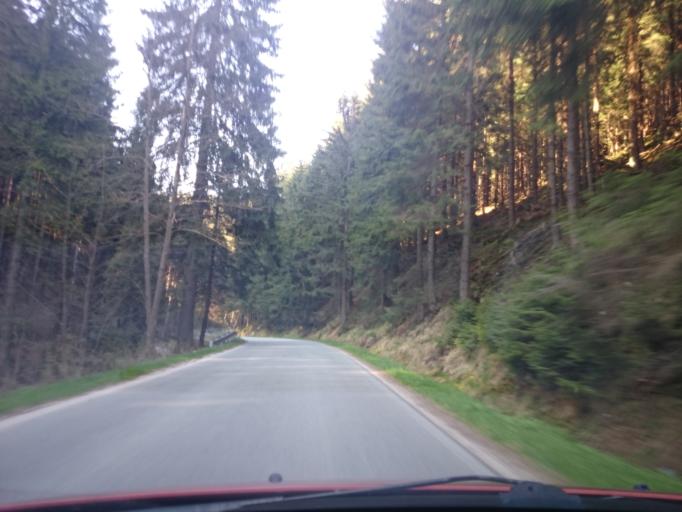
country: PL
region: Lower Silesian Voivodeship
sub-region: Powiat klodzki
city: Duszniki-Zdroj
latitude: 50.3758
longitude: 16.3938
